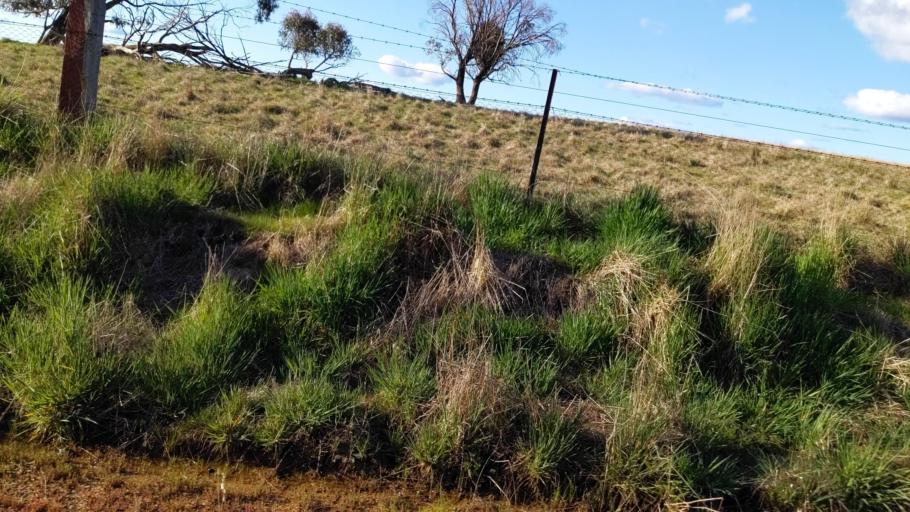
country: AU
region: New South Wales
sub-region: Blayney
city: Millthorpe
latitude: -33.3969
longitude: 149.3109
